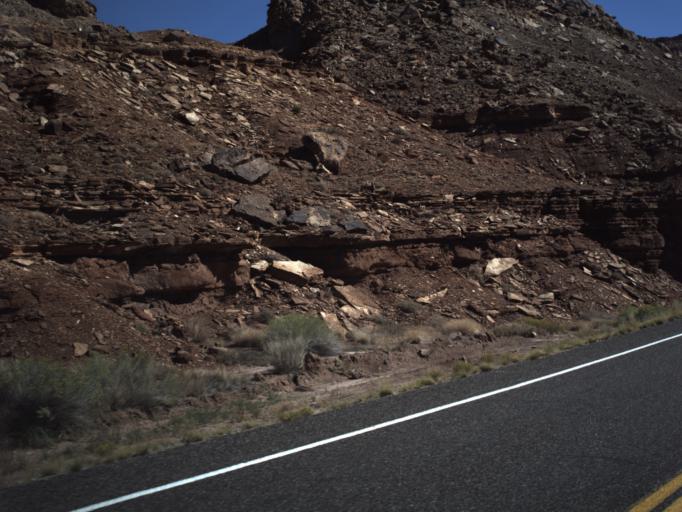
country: US
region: Utah
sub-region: San Juan County
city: Blanding
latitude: 37.8939
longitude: -110.4431
